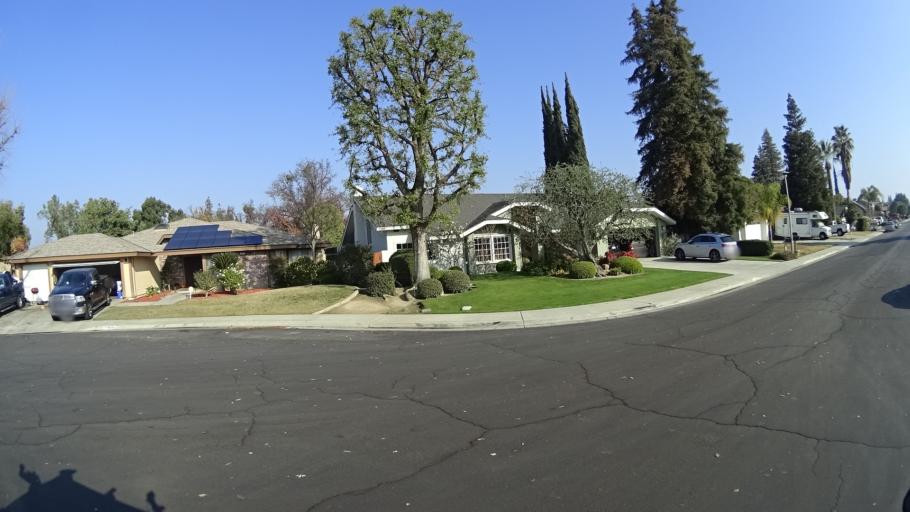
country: US
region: California
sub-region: Kern County
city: Greenacres
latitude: 35.3382
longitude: -119.0918
